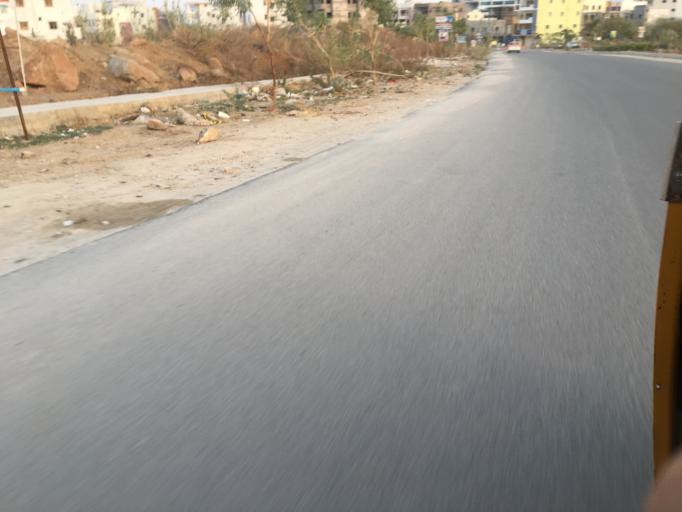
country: IN
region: Telangana
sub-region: Medak
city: Serilingampalle
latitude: 17.4310
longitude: 78.3312
